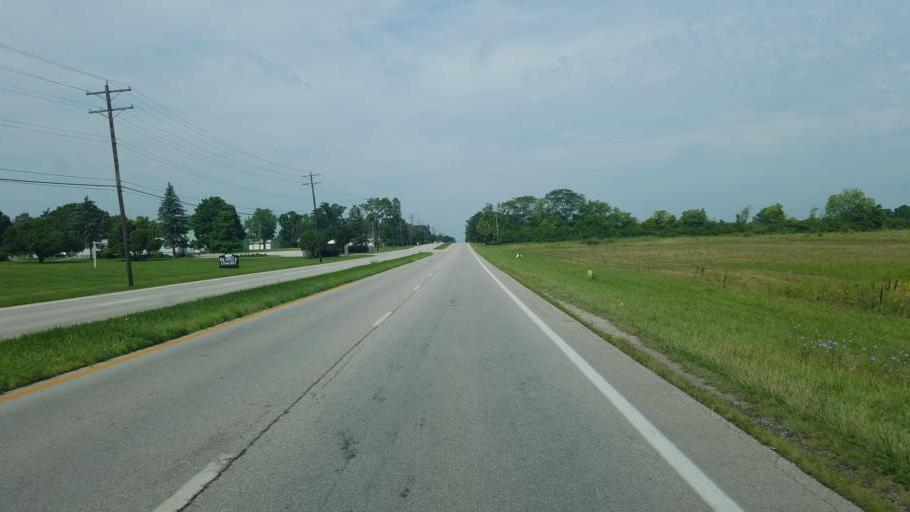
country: US
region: Ohio
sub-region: Franklin County
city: Lake Darby
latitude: 39.9499
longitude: -83.1836
